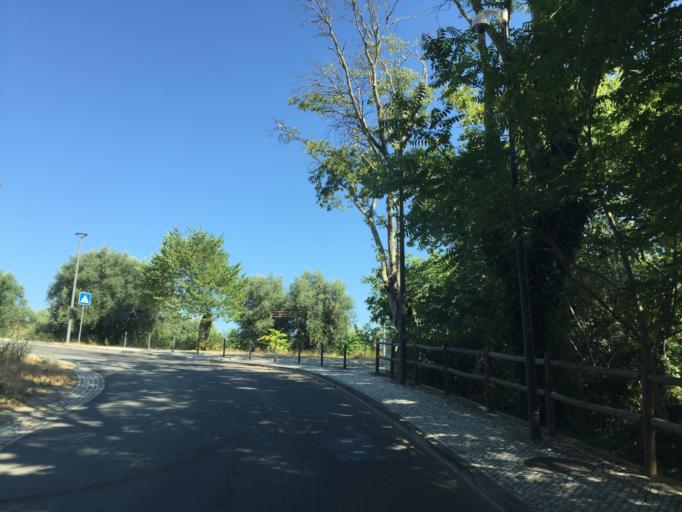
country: PT
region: Santarem
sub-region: Tomar
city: Tomar
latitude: 39.6051
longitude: -8.4175
